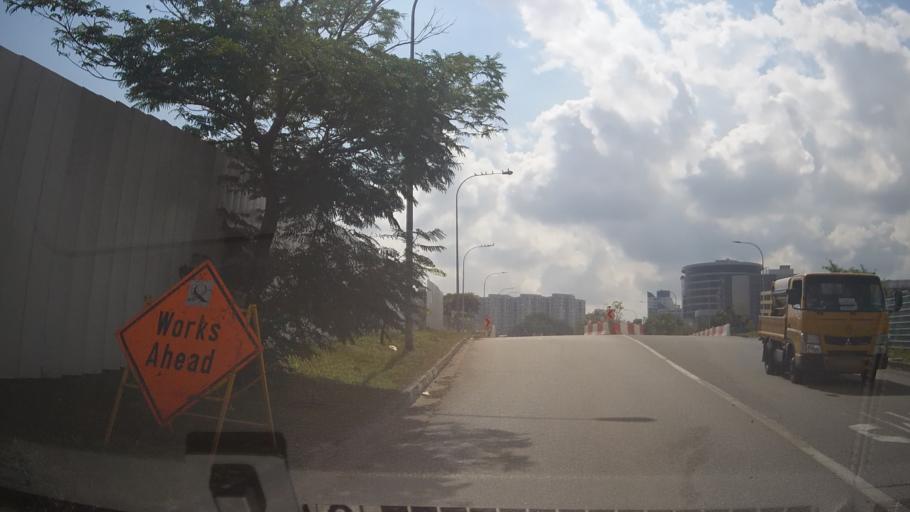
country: MY
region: Johor
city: Kampung Pasir Gudang Baru
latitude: 1.3828
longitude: 103.9291
